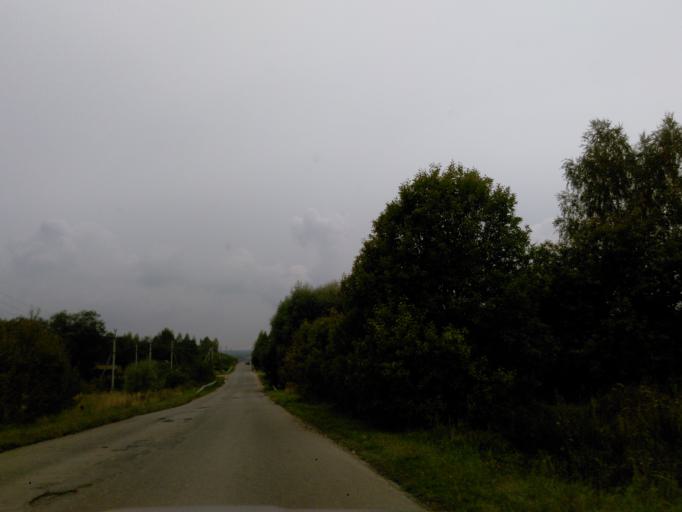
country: RU
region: Moskovskaya
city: Mendeleyevo
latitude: 56.1061
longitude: 37.2538
